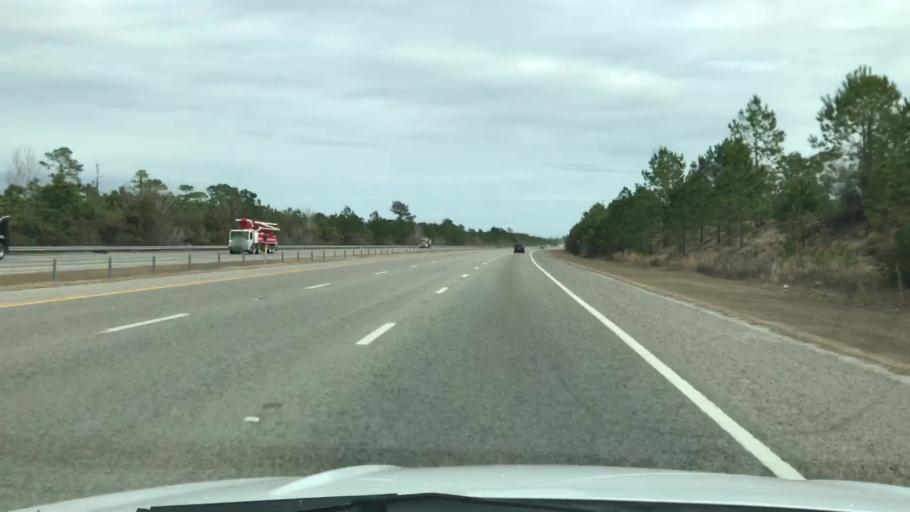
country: US
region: South Carolina
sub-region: Horry County
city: Forestbrook
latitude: 33.7238
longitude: -78.9922
